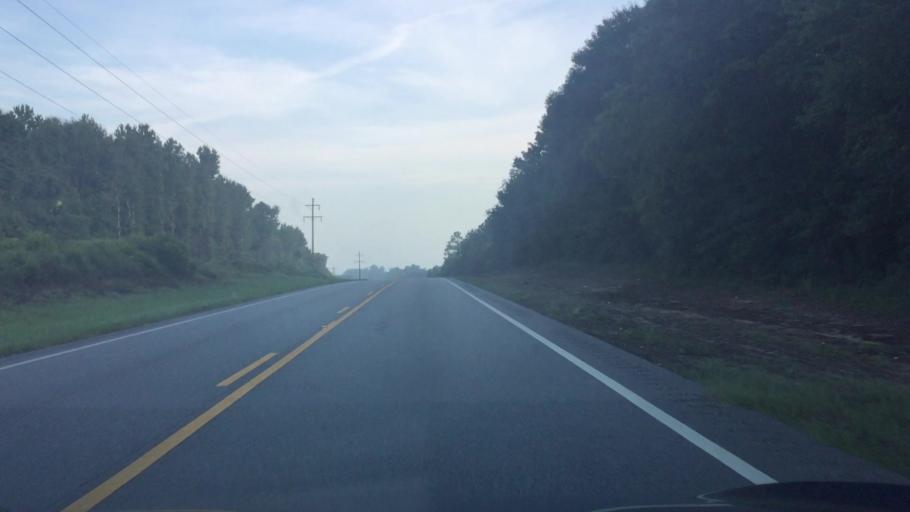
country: US
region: Alabama
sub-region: Covington County
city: Florala
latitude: 31.0684
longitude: -86.4019
